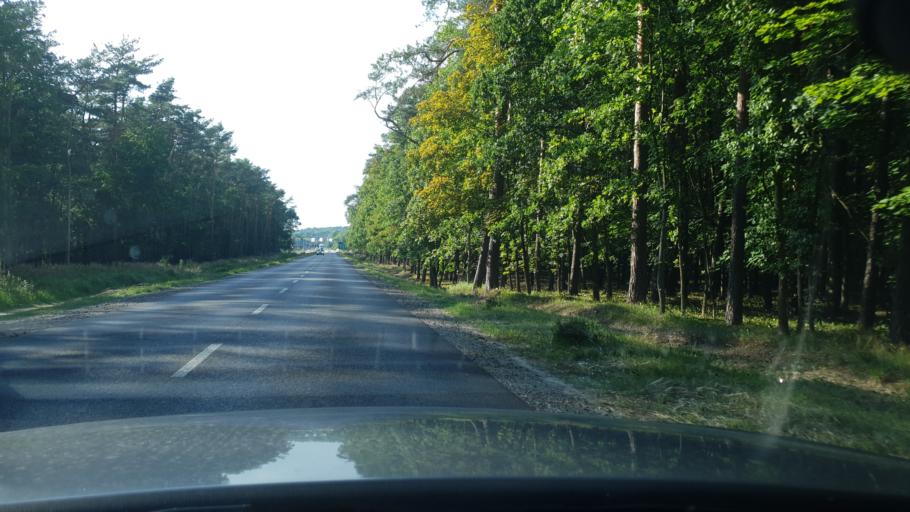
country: PL
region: Kujawsko-Pomorskie
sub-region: Grudziadz
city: Grudziadz
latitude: 53.4480
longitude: 18.7400
